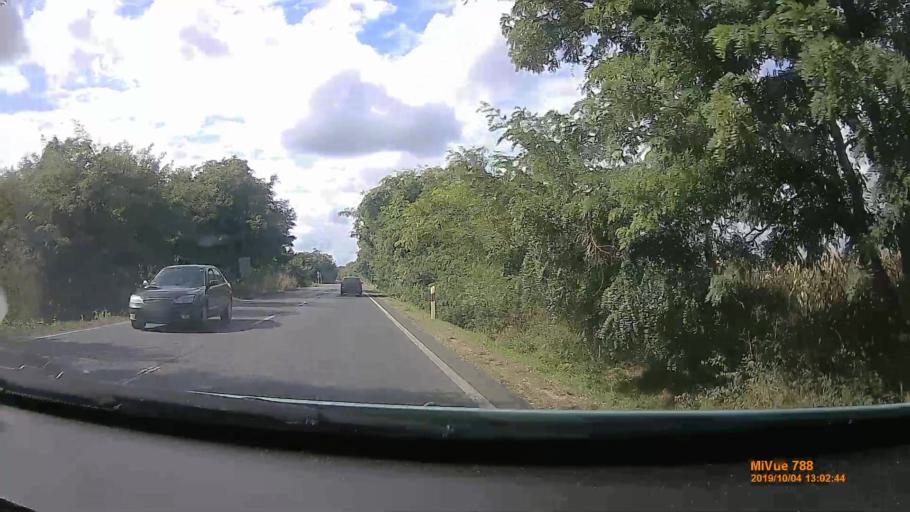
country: HU
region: Szabolcs-Szatmar-Bereg
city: Nyirtelek
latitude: 47.9573
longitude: 21.6474
